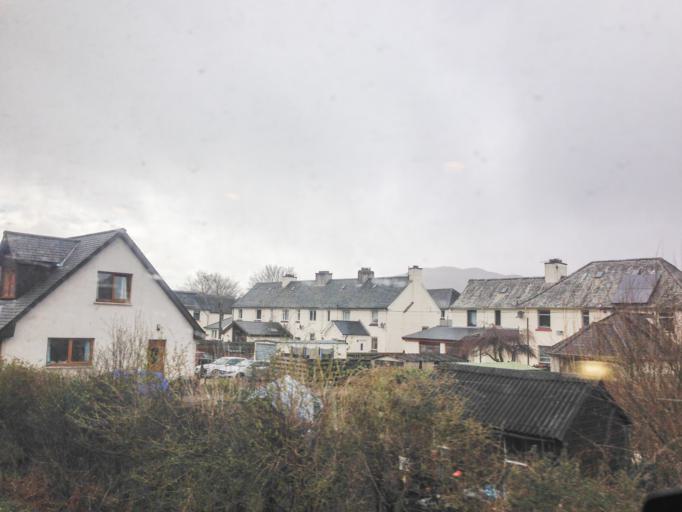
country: GB
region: Scotland
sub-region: Highland
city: Fort William
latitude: 56.8264
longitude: -5.0890
